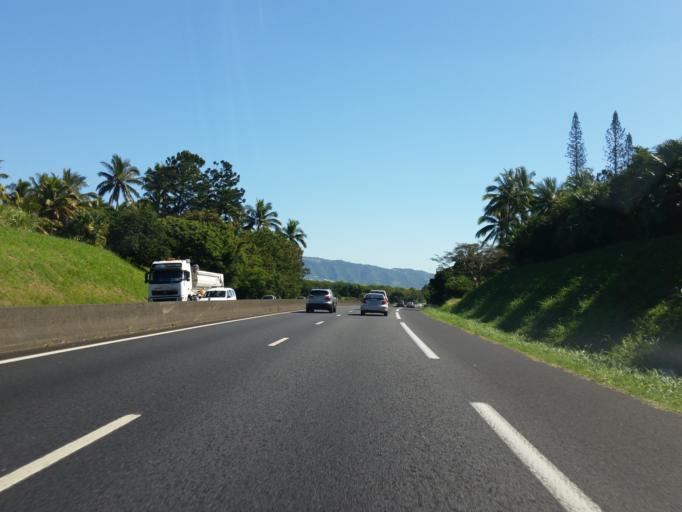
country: RE
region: Reunion
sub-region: Reunion
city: Sainte-Marie
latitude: -20.9029
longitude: 55.5383
